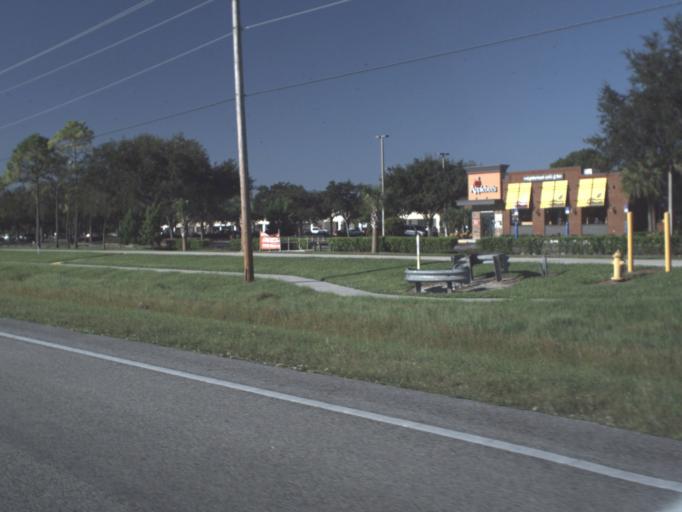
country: US
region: Florida
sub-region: Lee County
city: Palmona Park
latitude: 26.6859
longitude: -81.9016
